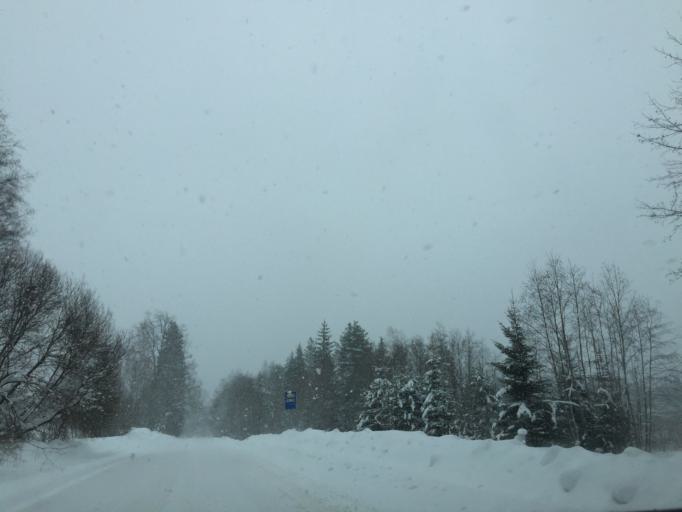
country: LV
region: Amatas Novads
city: Drabesi
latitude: 57.0856
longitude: 25.3609
